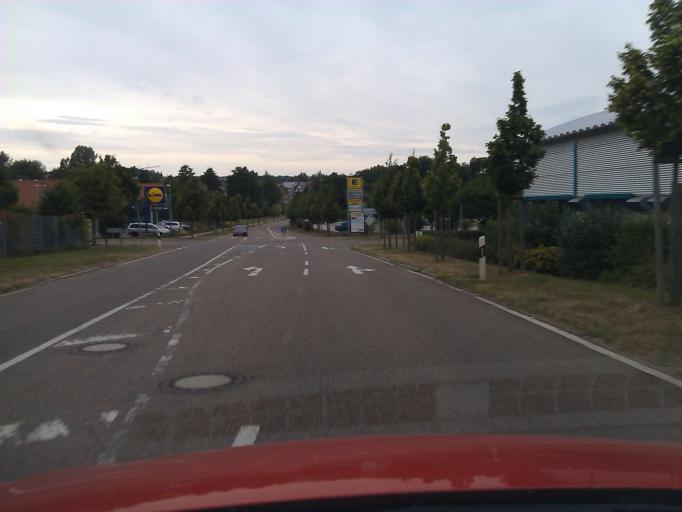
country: DE
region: Baden-Wuerttemberg
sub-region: Regierungsbezirk Stuttgart
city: Guglingen
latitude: 49.0624
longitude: 9.0065
